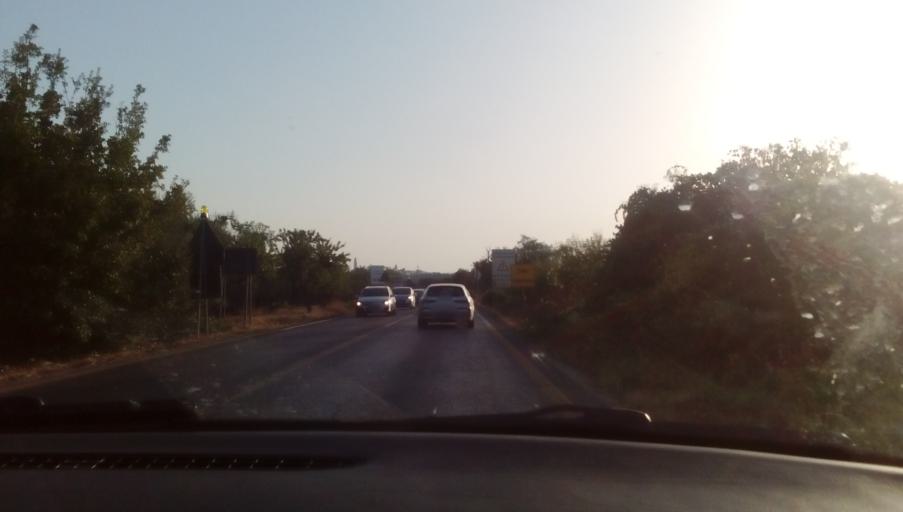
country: IT
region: Apulia
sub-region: Provincia di Bari
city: Palo del Colle
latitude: 41.0667
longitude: 16.7260
